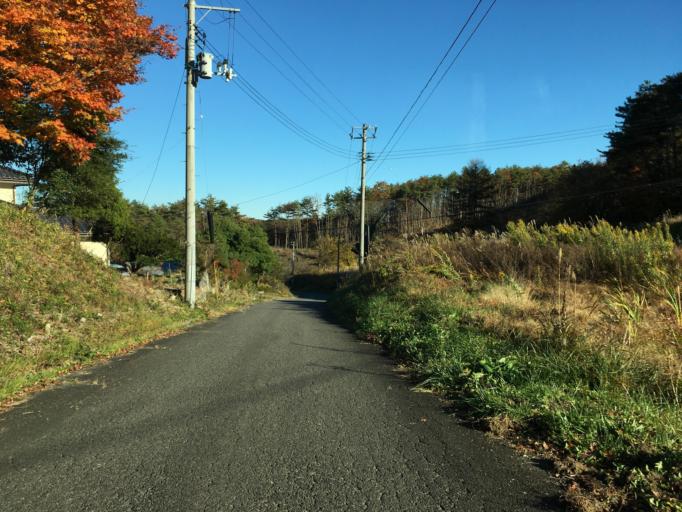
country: JP
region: Fukushima
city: Ishikawa
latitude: 37.2396
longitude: 140.5285
